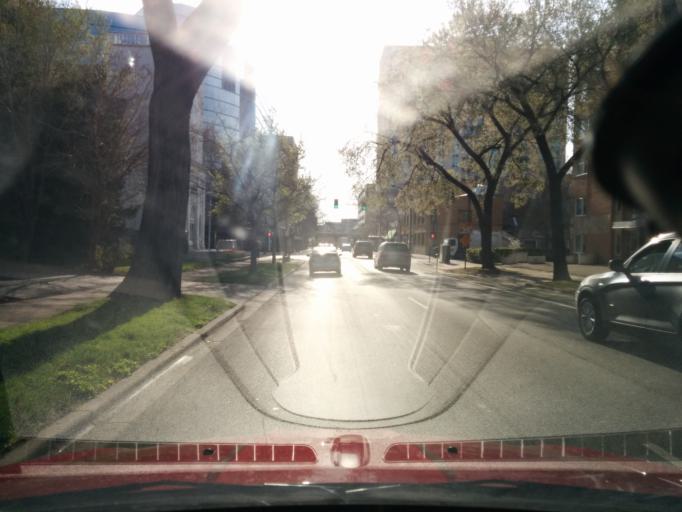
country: US
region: Illinois
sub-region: Cook County
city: Evanston
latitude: 42.0486
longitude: -87.6877
